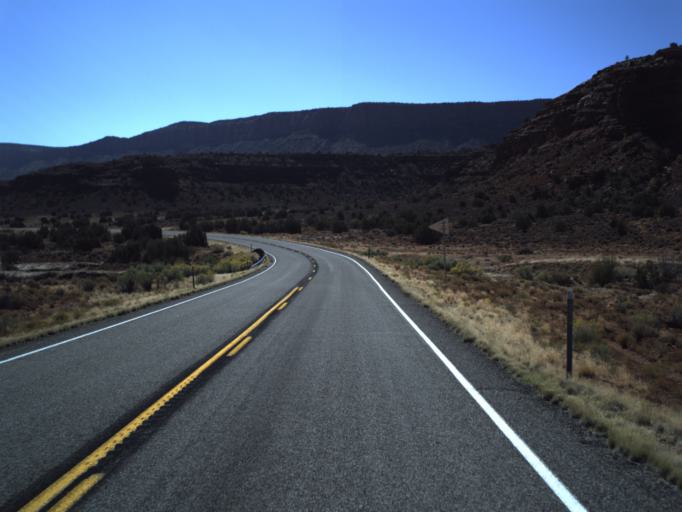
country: US
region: Utah
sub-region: San Juan County
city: Blanding
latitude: 37.7092
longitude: -110.2422
